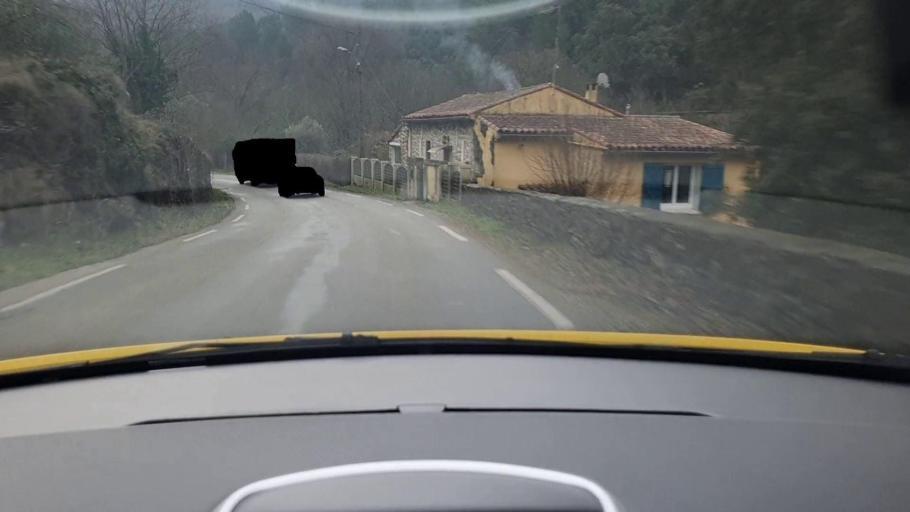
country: FR
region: Languedoc-Roussillon
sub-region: Departement du Gard
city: Besseges
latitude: 44.2796
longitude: 4.1047
